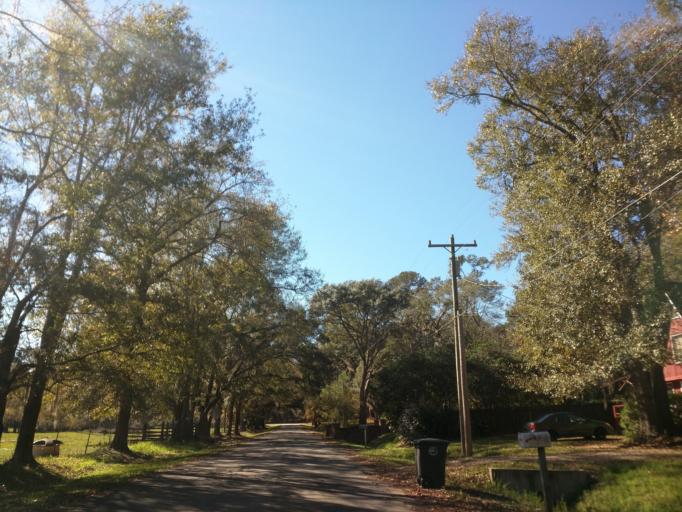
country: US
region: Florida
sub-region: Leon County
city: Tallahassee
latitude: 30.4972
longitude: -84.3134
